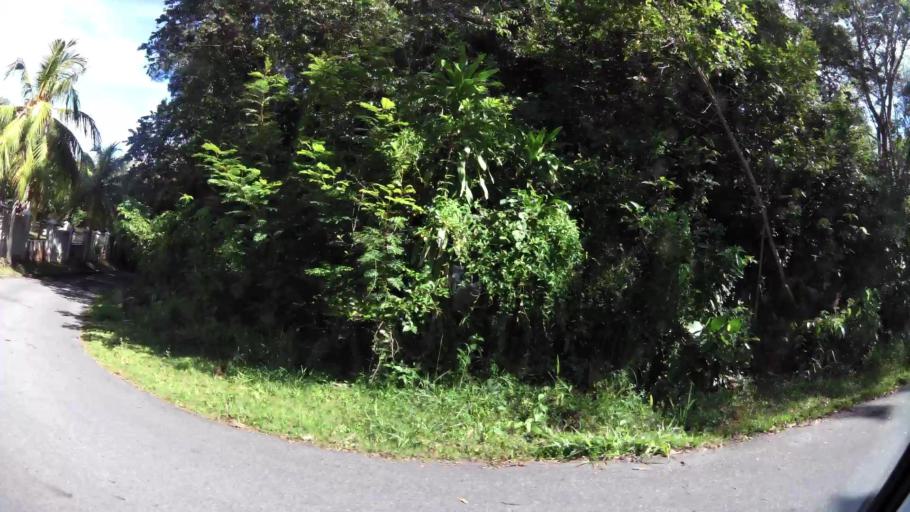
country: BN
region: Brunei and Muara
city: Bandar Seri Begawan
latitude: 4.9531
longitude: 114.9407
